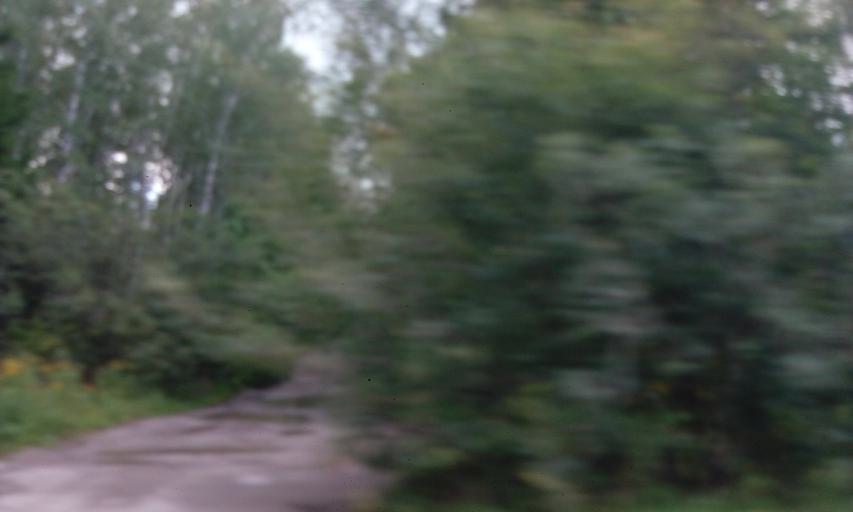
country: RU
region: Novosibirsk
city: Akademgorodok
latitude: 54.8427
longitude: 83.1335
